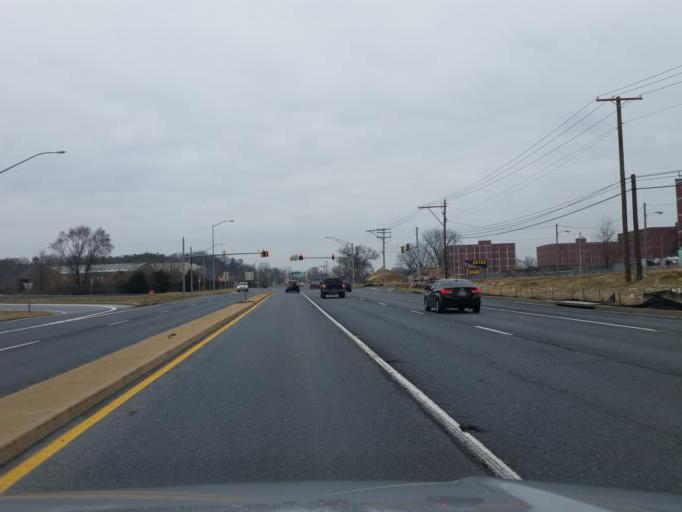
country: US
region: Maryland
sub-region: Howard County
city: Elkridge
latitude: 39.2218
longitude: -76.7010
